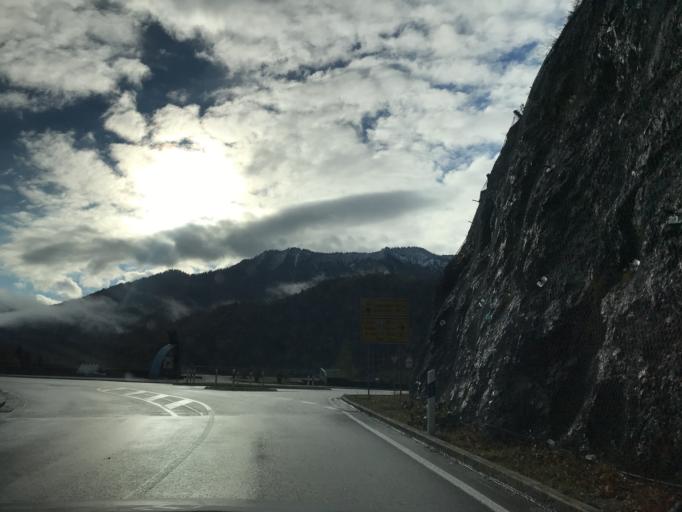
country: DE
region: Bavaria
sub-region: Upper Bavaria
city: Lenggries
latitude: 47.5863
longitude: 11.5479
